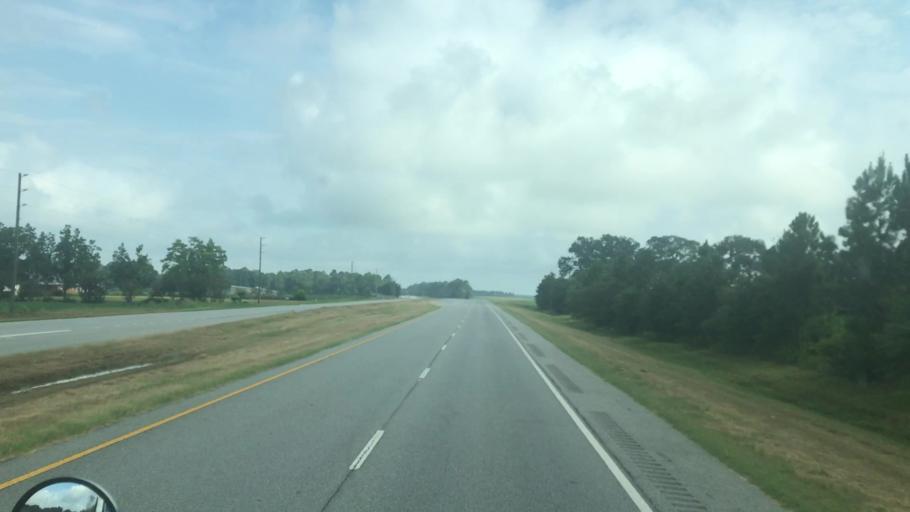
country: US
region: Georgia
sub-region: Miller County
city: Colquitt
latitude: 31.1819
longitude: -84.7617
